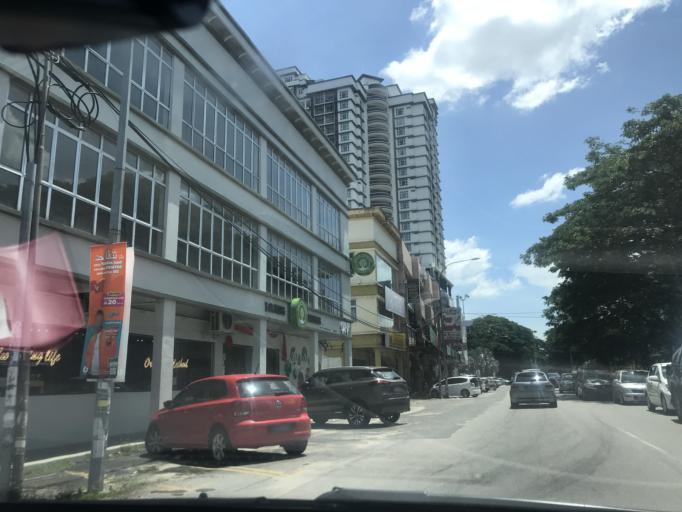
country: MY
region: Kelantan
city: Kota Bharu
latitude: 6.1285
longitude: 102.2472
